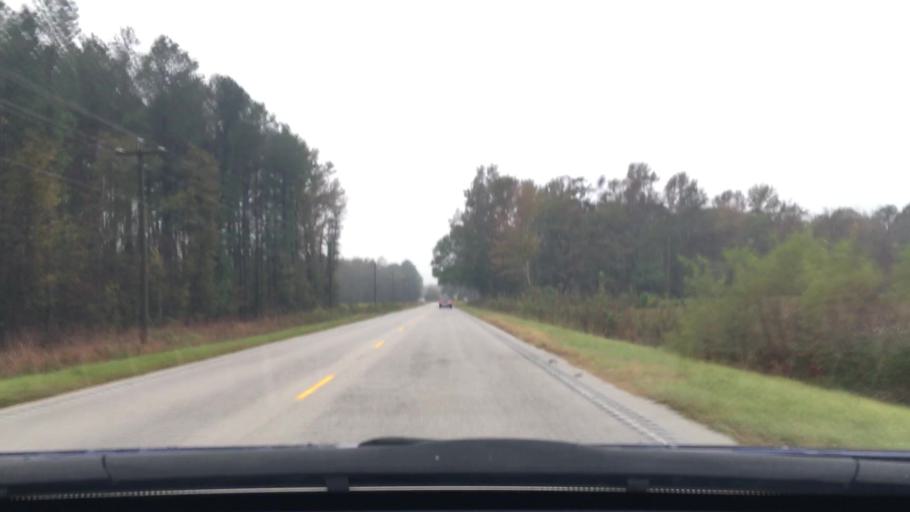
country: US
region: South Carolina
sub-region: Florence County
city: Timmonsville
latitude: 34.2284
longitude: -79.9909
